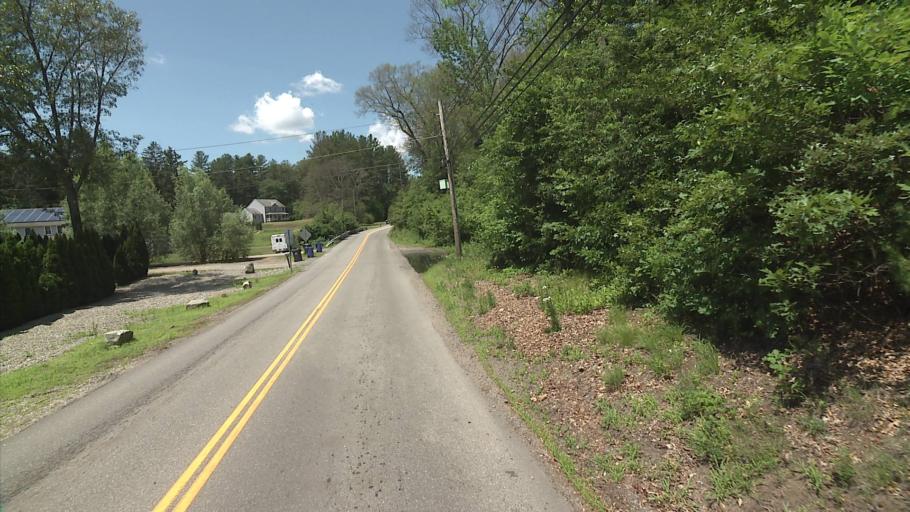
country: US
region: Connecticut
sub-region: New London County
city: Jewett City
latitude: 41.6128
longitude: -71.9393
